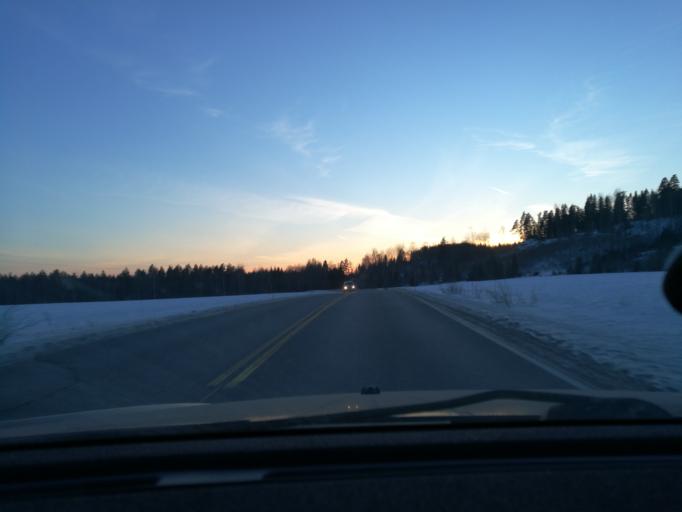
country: FI
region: Uusimaa
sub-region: Helsinki
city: Vihti
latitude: 60.4243
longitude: 24.3675
